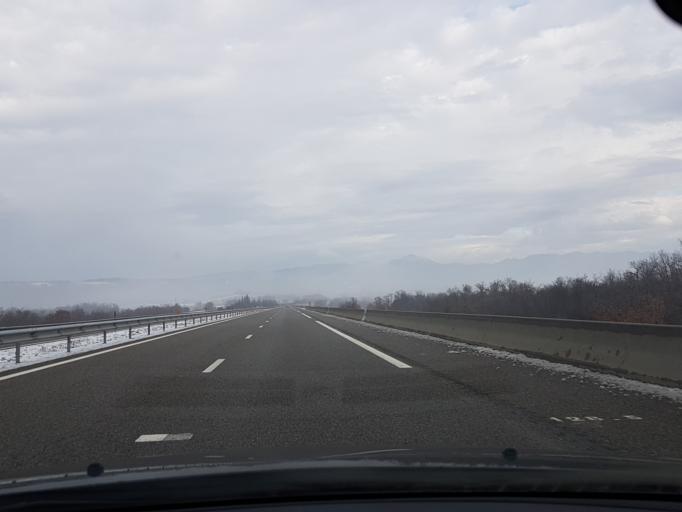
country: FR
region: Provence-Alpes-Cote d'Azur
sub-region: Departement des Alpes-de-Haute-Provence
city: Sisteron
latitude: 44.2681
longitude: 5.9041
